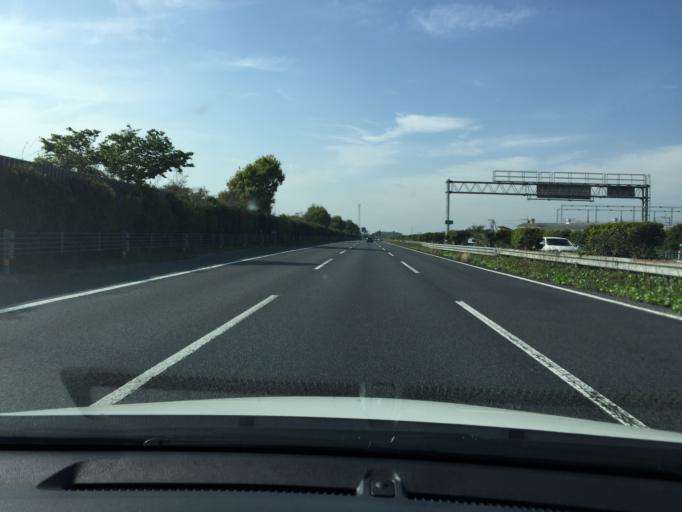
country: JP
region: Tochigi
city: Utsunomiya-shi
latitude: 36.6147
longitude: 139.8434
